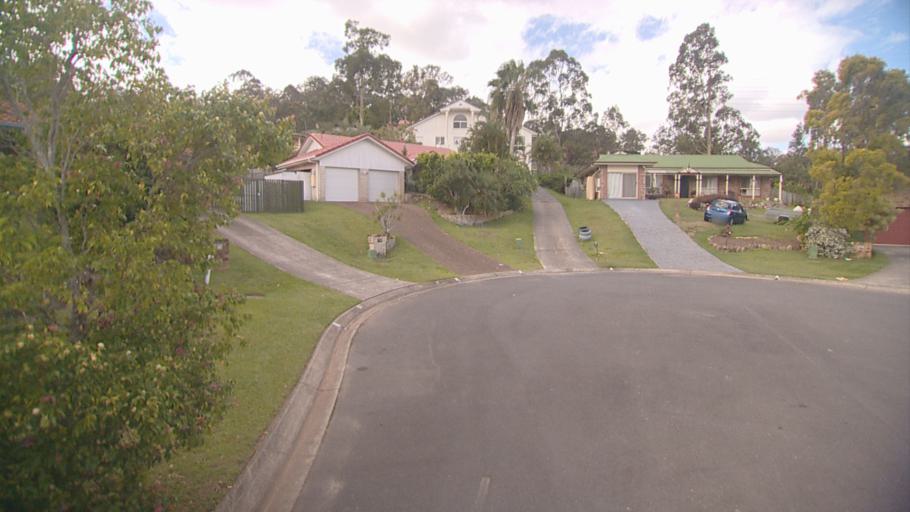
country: AU
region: Queensland
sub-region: Logan
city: Slacks Creek
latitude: -27.6768
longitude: 153.1742
